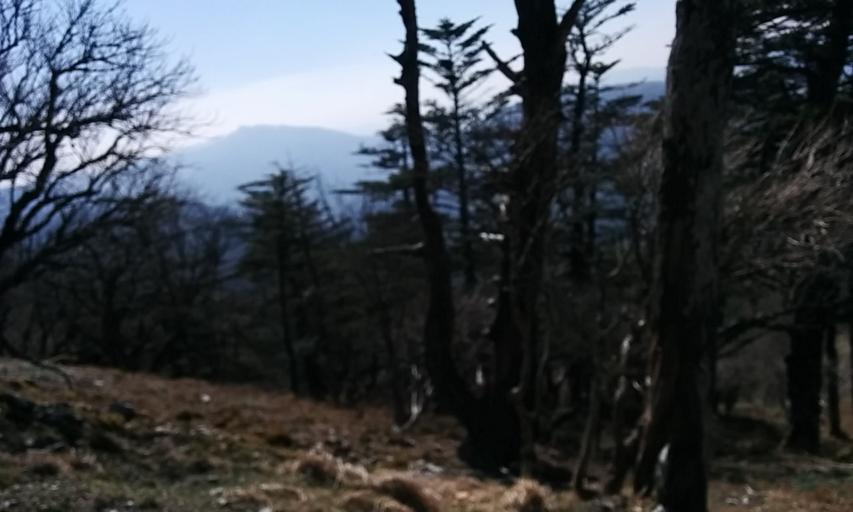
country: JP
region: Tokushima
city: Wakimachi
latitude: 33.8580
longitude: 134.0952
